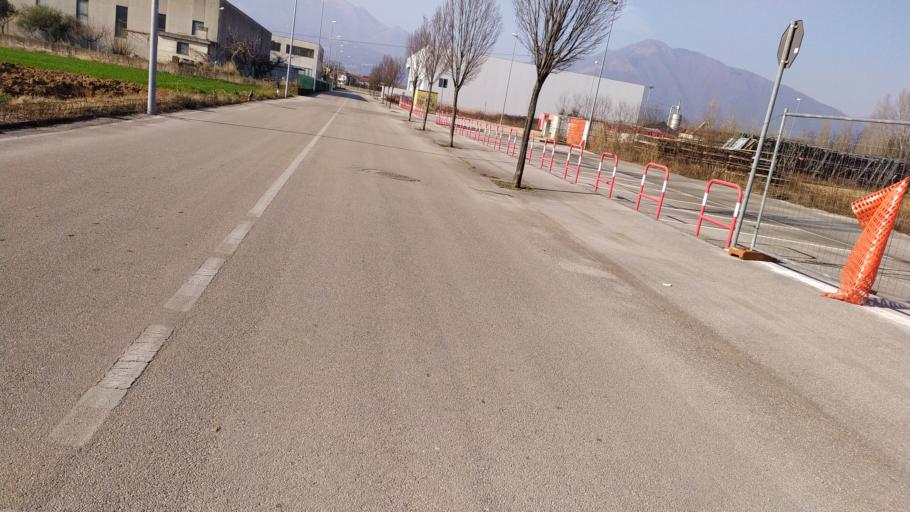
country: IT
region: Veneto
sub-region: Provincia di Vicenza
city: San Vito di Leguzzano
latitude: 45.6852
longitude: 11.4039
